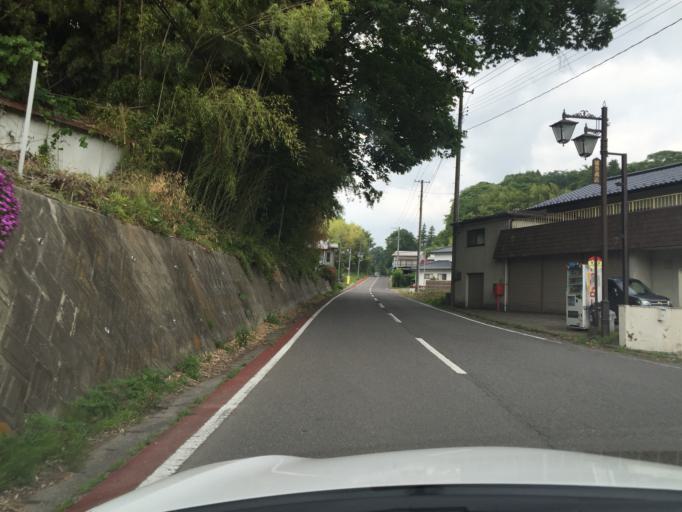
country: JP
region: Fukushima
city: Sukagawa
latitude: 37.2349
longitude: 140.4490
